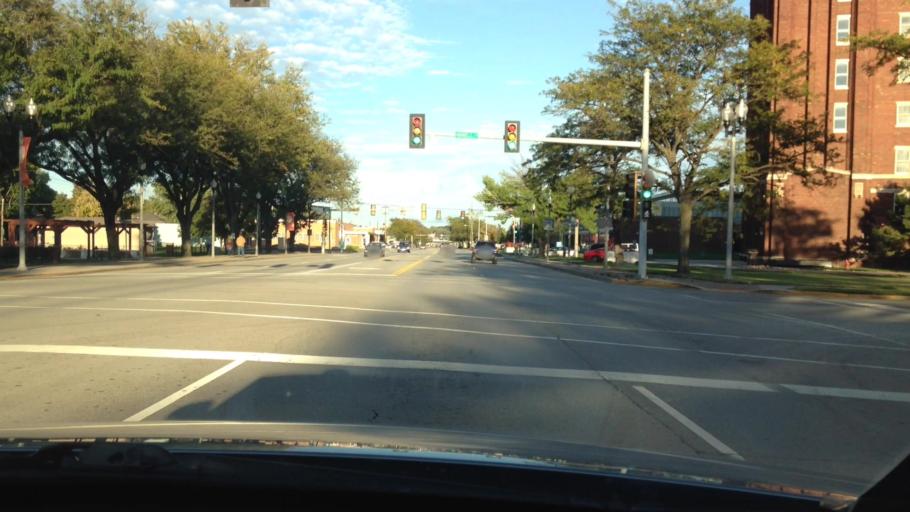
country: US
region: Missouri
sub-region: Clay County
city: North Kansas City
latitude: 39.1427
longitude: -94.5727
